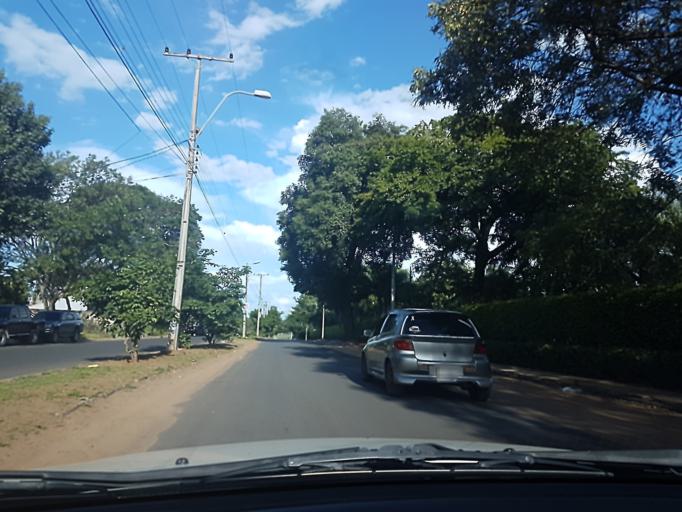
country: PY
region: Central
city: Colonia Mariano Roque Alonso
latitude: -25.2108
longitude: -57.5191
